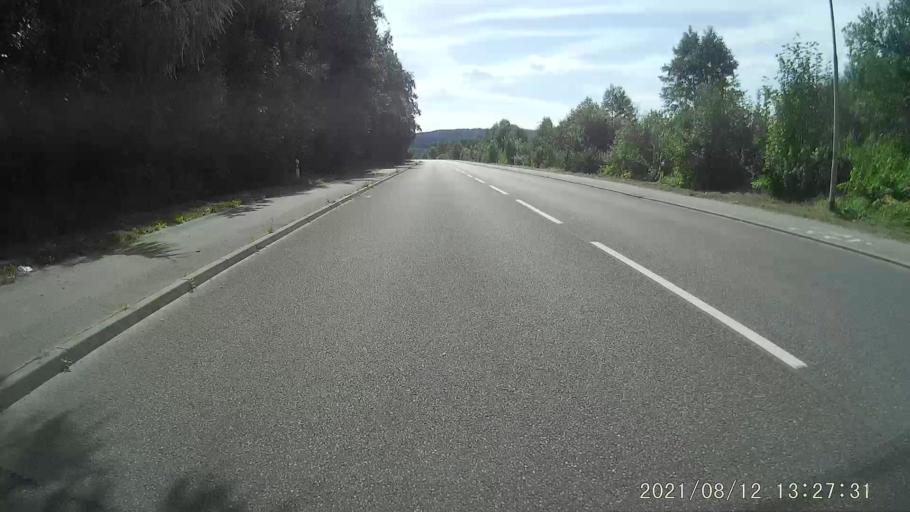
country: PL
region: Lower Silesian Voivodeship
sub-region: Powiat klodzki
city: Ladek-Zdroj
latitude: 50.3354
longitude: 16.8697
